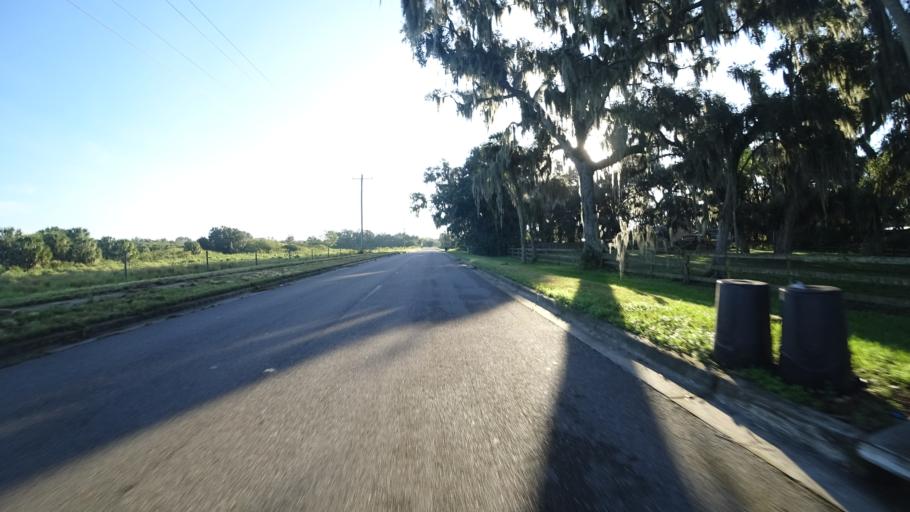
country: US
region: Florida
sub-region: Manatee County
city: Ellenton
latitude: 27.5400
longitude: -82.5390
